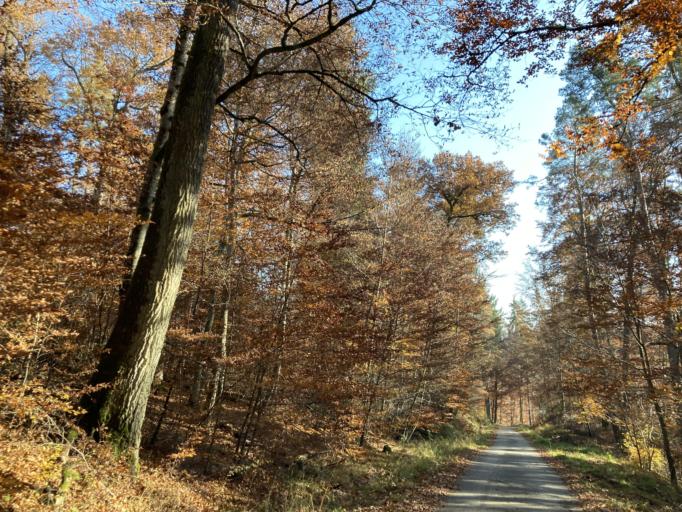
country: DE
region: Baden-Wuerttemberg
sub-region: Tuebingen Region
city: Tuebingen
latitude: 48.5668
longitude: 9.0632
